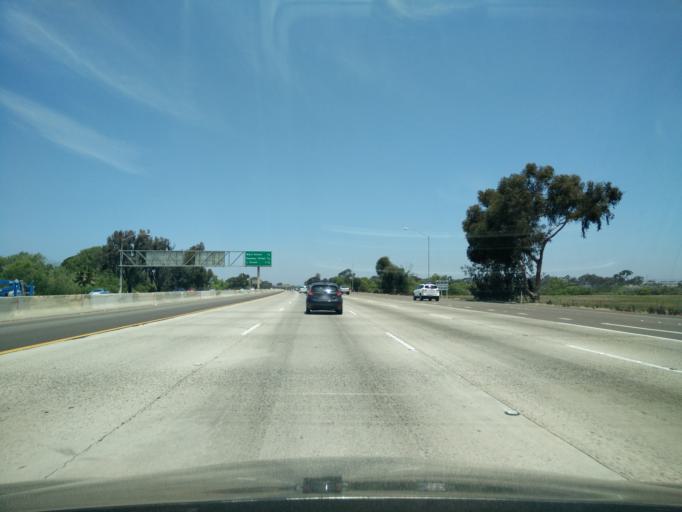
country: US
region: California
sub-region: San Diego County
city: Imperial Beach
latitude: 32.5870
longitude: -117.0875
